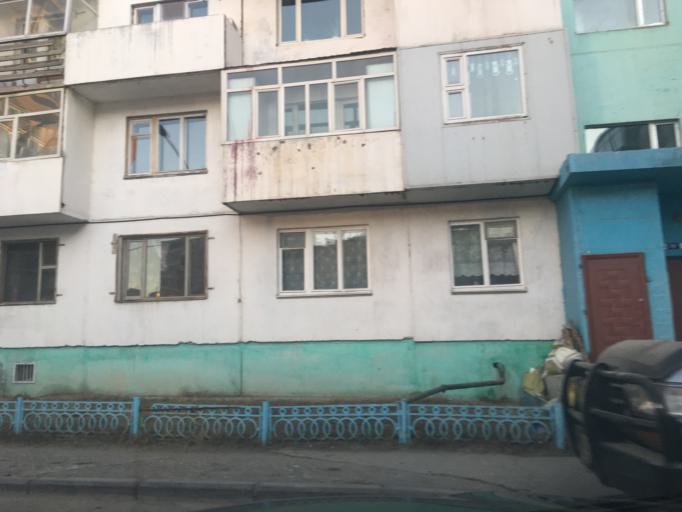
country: MN
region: Ulaanbaatar
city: Ulaanbaatar
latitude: 47.9189
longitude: 106.8794
